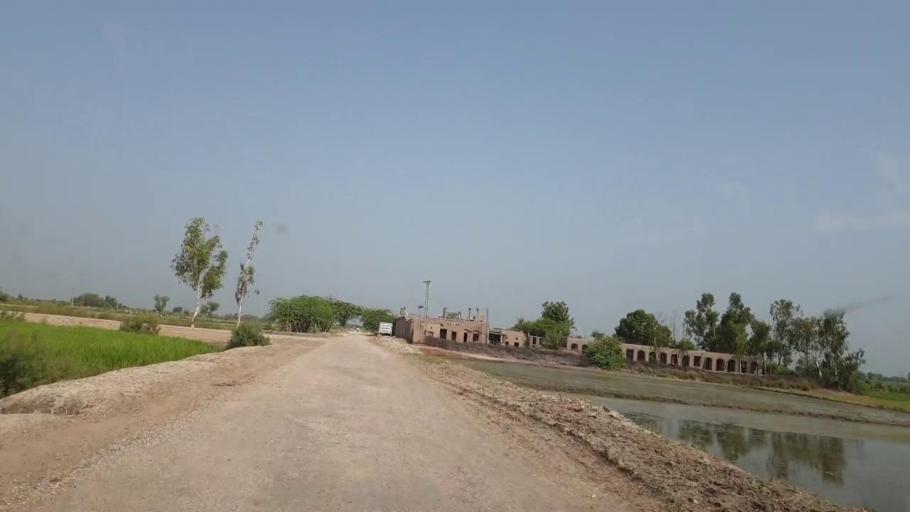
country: PK
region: Sindh
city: Lakhi
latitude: 27.8292
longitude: 68.6855
